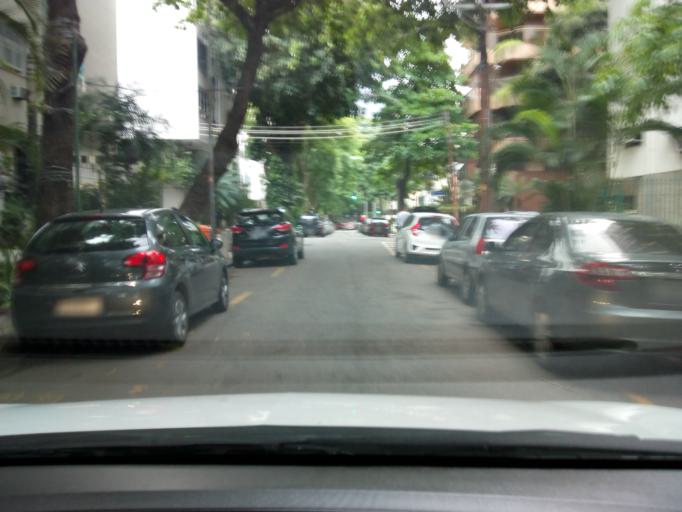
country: BR
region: Rio de Janeiro
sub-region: Rio De Janeiro
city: Rio de Janeiro
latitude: -22.9840
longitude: -43.2243
